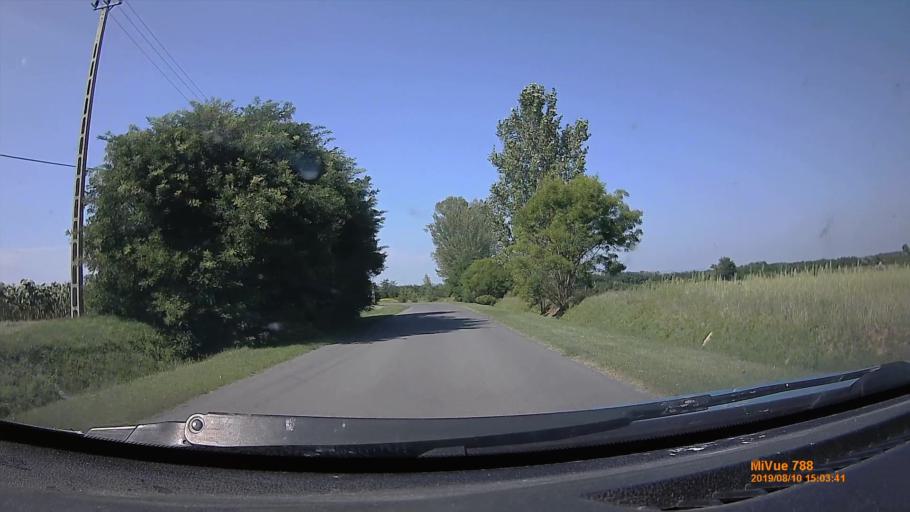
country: HU
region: Somogy
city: Lengyeltoti
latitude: 46.6686
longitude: 17.5716
